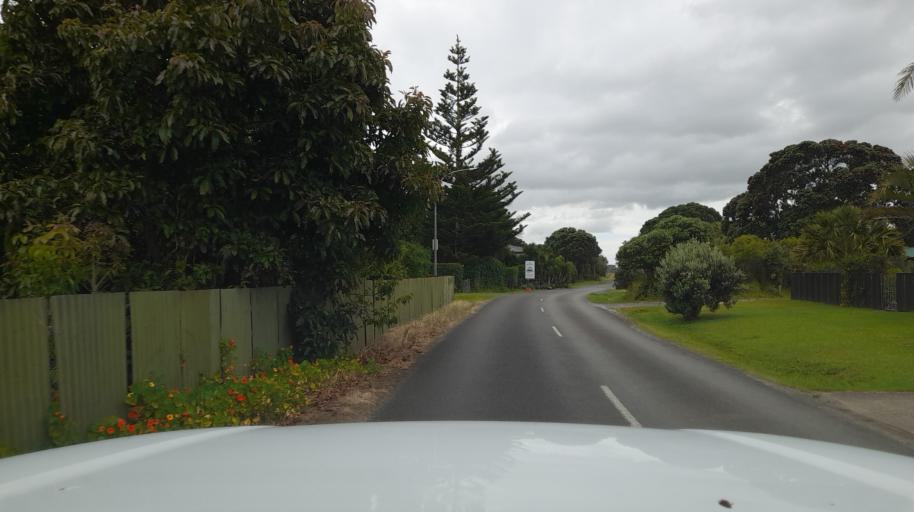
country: NZ
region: Northland
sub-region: Far North District
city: Ahipara
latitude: -35.1609
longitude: 173.1594
